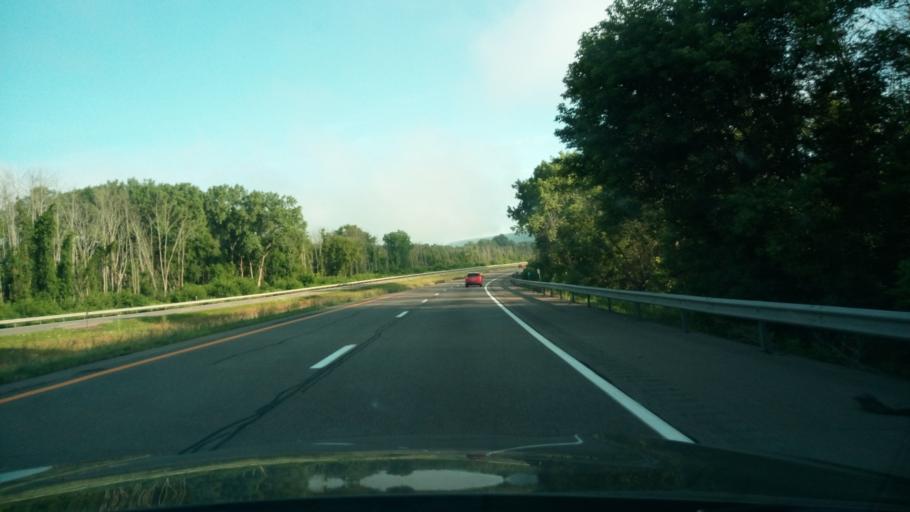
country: US
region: New York
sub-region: Steuben County
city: Bath
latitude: 42.2731
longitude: -77.2233
